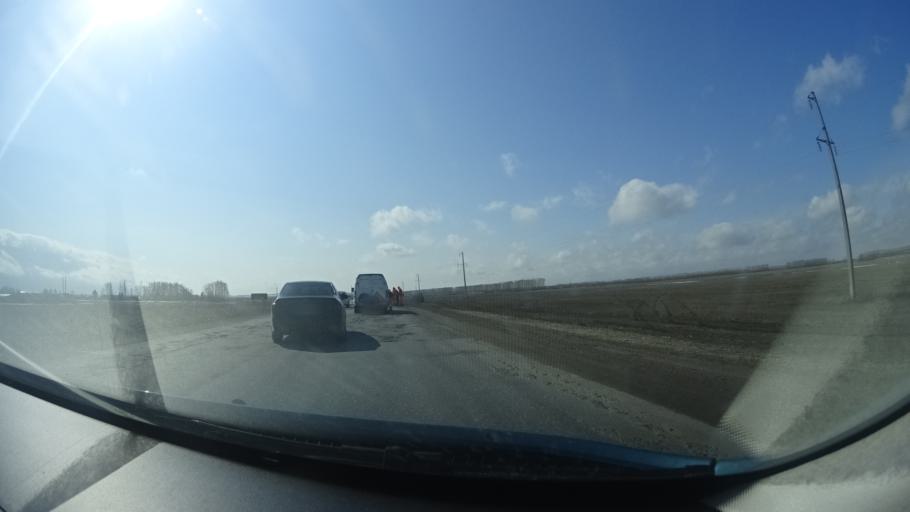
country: RU
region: Bashkortostan
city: Mikhaylovka
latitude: 54.9553
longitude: 55.7563
